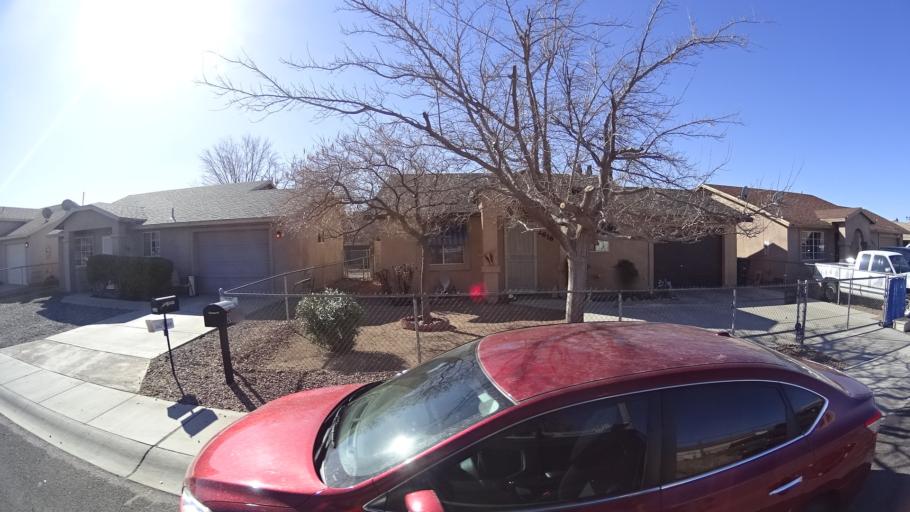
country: US
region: Arizona
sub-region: Mohave County
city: Kingman
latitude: 35.2014
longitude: -114.0175
